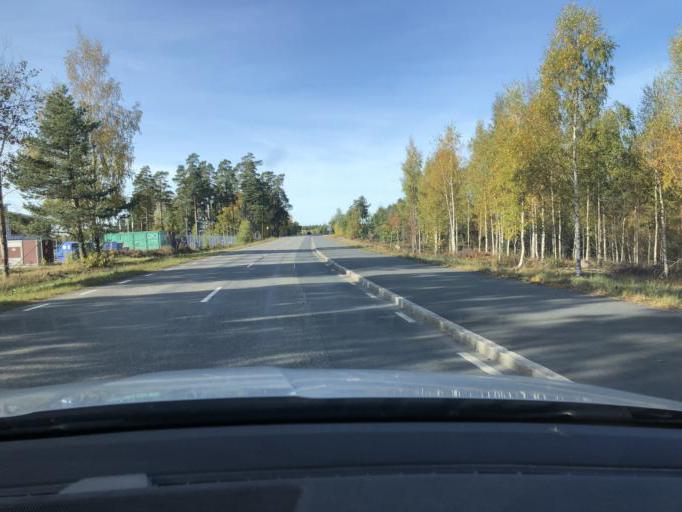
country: SE
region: Joenkoeping
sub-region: Jonkopings Kommun
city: Jonkoping
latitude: 57.7718
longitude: 14.0920
